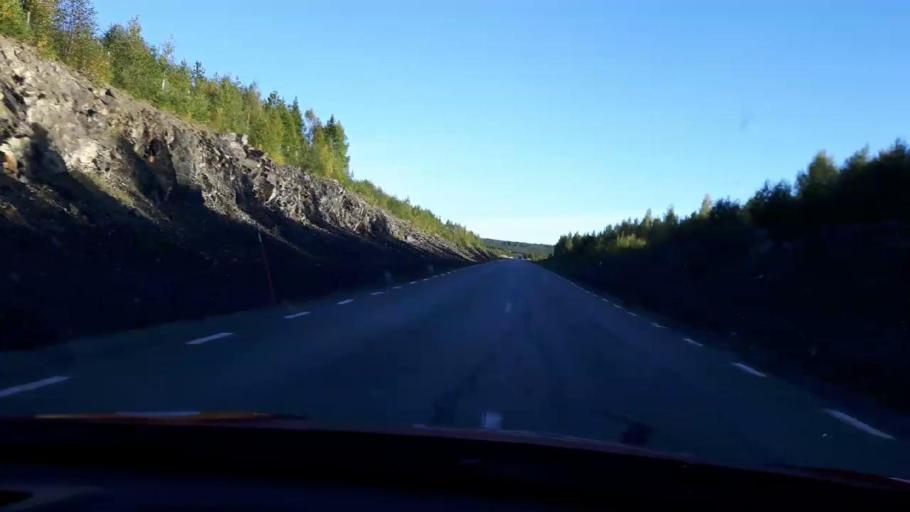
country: SE
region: Jaemtland
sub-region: OEstersunds Kommun
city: Lit
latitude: 63.7776
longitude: 14.7091
